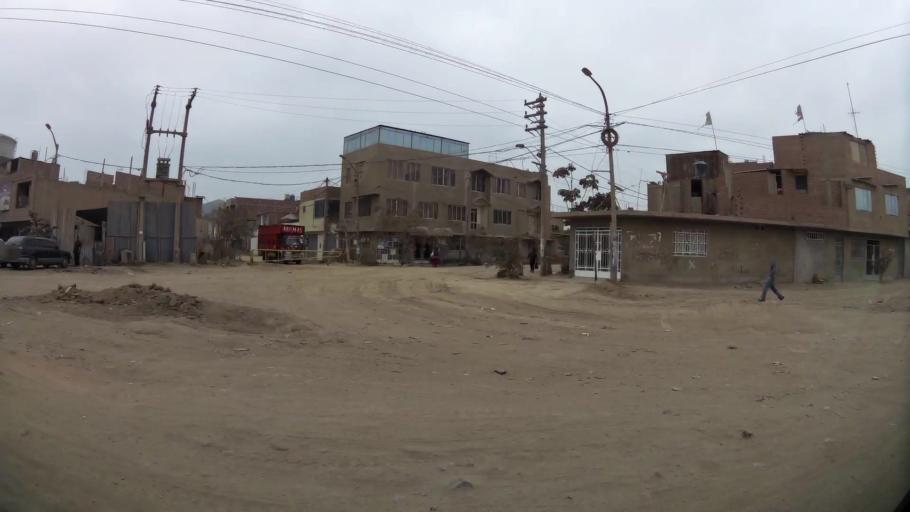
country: PE
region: Lima
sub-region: Lima
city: Independencia
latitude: -11.9558
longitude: -77.0901
